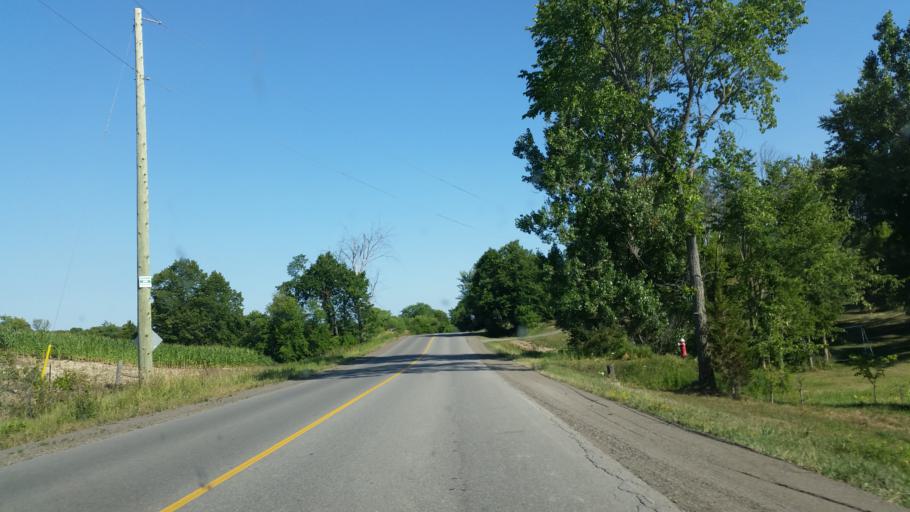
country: CA
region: Ontario
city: Bradford West Gwillimbury
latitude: 43.9460
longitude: -79.7578
